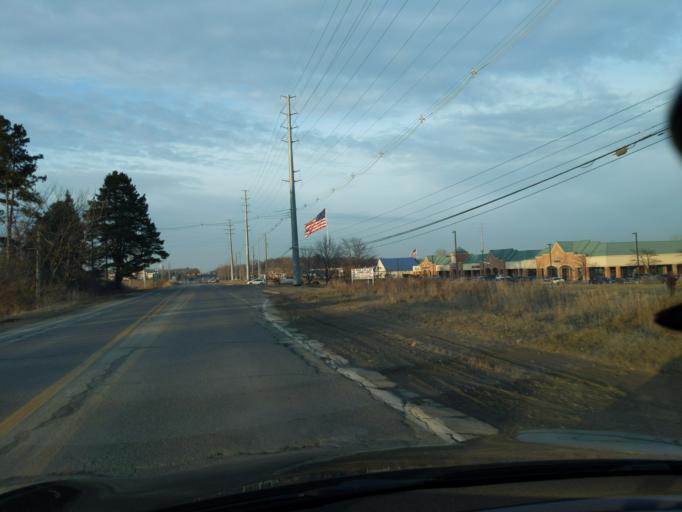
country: US
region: Michigan
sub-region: Livingston County
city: Brighton
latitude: 42.6294
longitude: -83.7527
